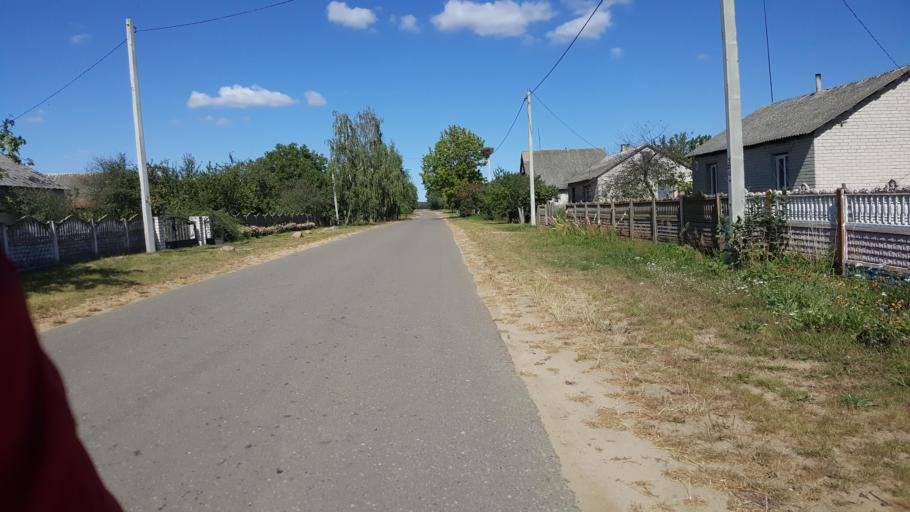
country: BY
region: Brest
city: Vysokaye
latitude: 52.2607
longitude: 23.4296
